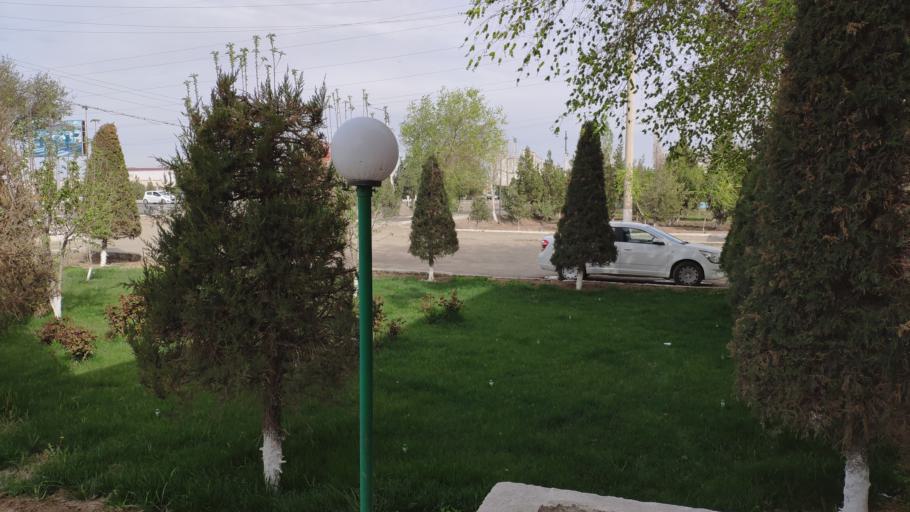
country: UZ
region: Xorazm
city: Urganch
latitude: 41.5321
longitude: 60.6670
